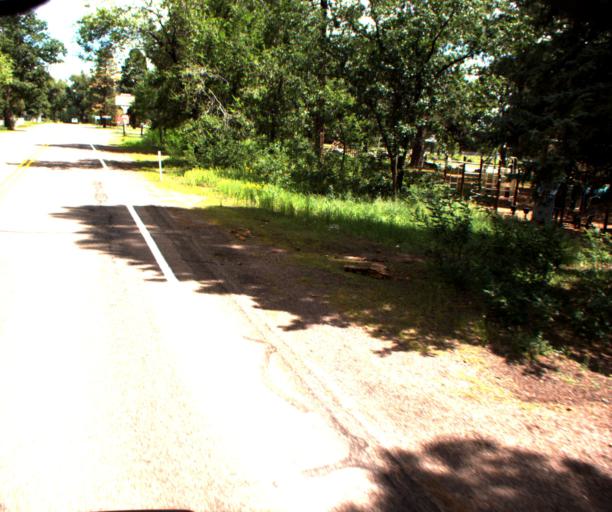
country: US
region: Arizona
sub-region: Navajo County
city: Pinetop-Lakeside
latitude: 34.0734
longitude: -109.8560
